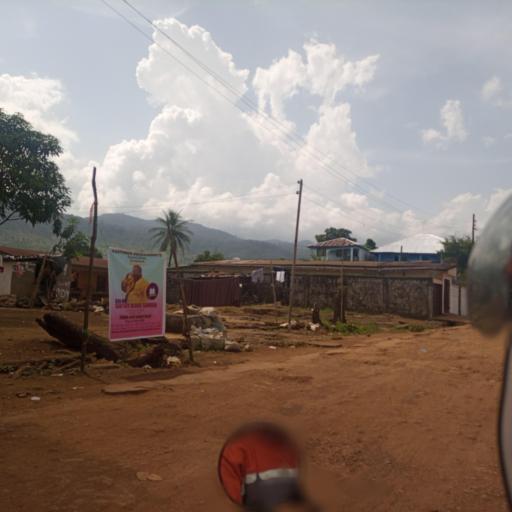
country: SL
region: Western Area
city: Hastings
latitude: 8.3848
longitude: -13.1443
